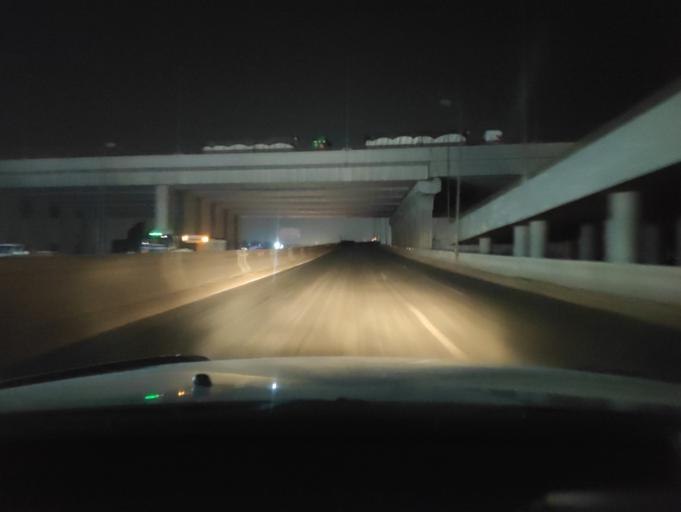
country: EG
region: Muhafazat al Qalyubiyah
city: Banha
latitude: 30.4972
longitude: 31.1667
